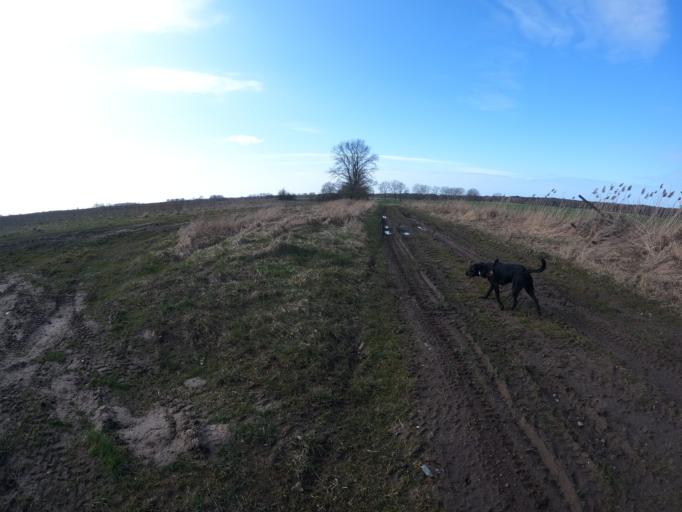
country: PL
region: West Pomeranian Voivodeship
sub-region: Powiat gryficki
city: Trzebiatow
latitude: 54.0952
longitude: 15.1935
